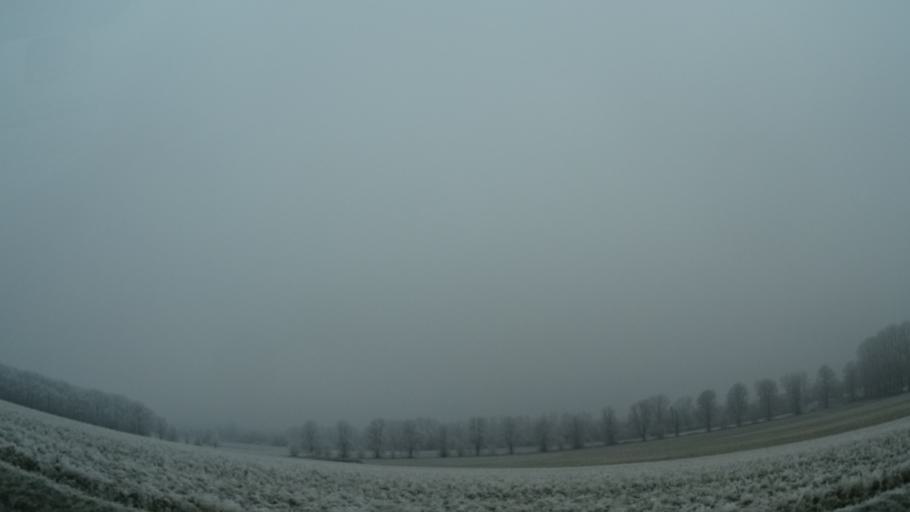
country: DE
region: Bavaria
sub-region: Regierungsbezirk Unterfranken
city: Hassfurt
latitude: 50.0244
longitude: 10.5026
